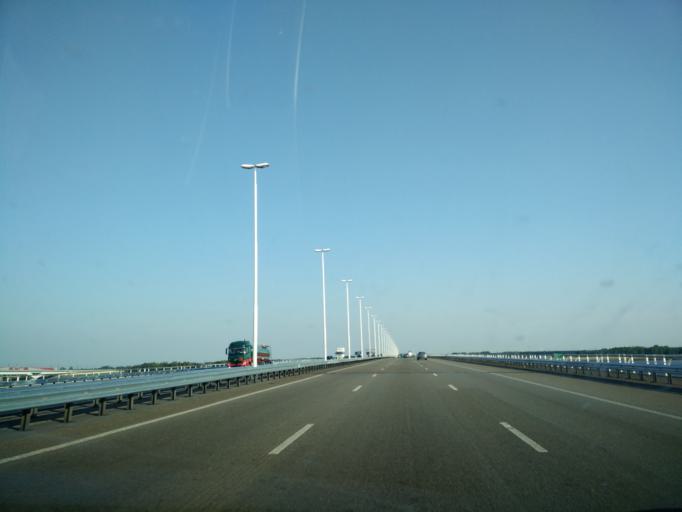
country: NL
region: South Holland
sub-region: Gemeente Strijen
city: Strijen
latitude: 51.7194
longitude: 4.6353
